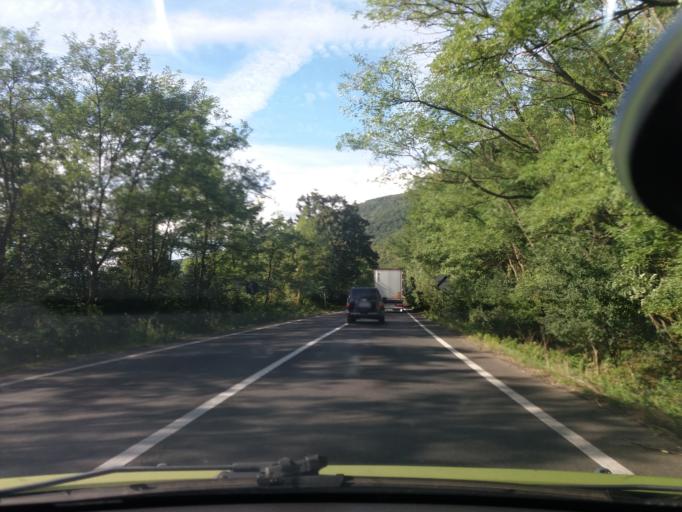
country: RO
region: Arad
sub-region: Comuna Savarsin
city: Savarsin
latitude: 46.0051
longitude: 22.2755
